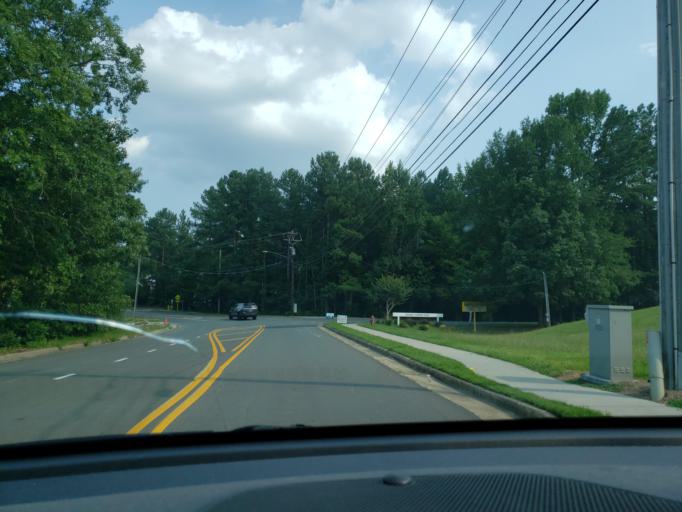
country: US
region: North Carolina
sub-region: Durham County
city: Durham
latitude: 35.9300
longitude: -78.9221
